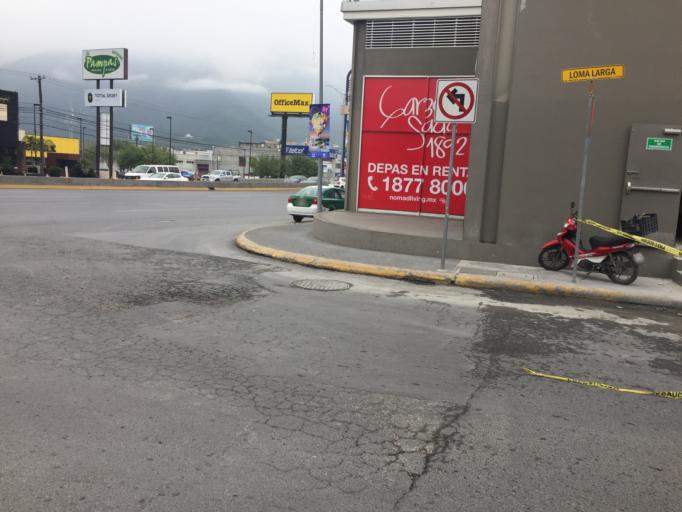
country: MX
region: Nuevo Leon
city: Guadalupe
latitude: 25.6409
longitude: -100.2861
